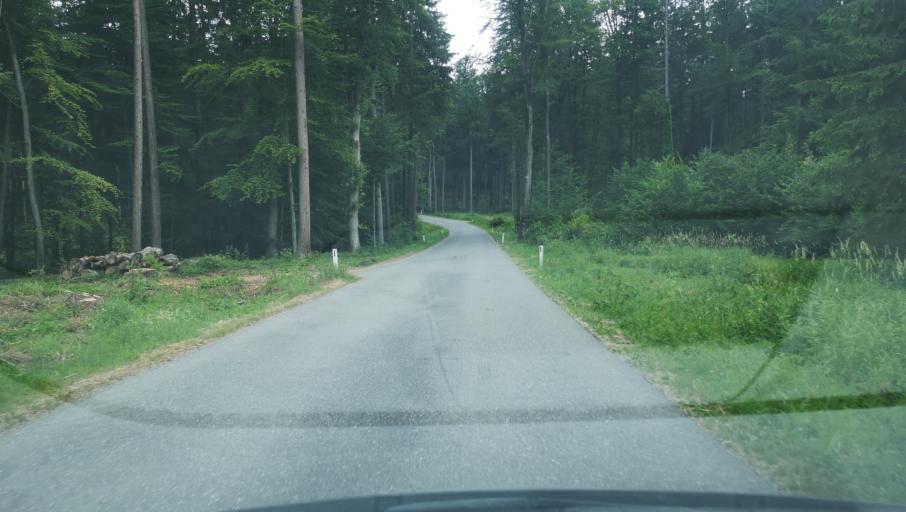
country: AT
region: Lower Austria
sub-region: Politischer Bezirk Melk
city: Blindenmarkt
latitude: 48.1666
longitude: 14.9721
